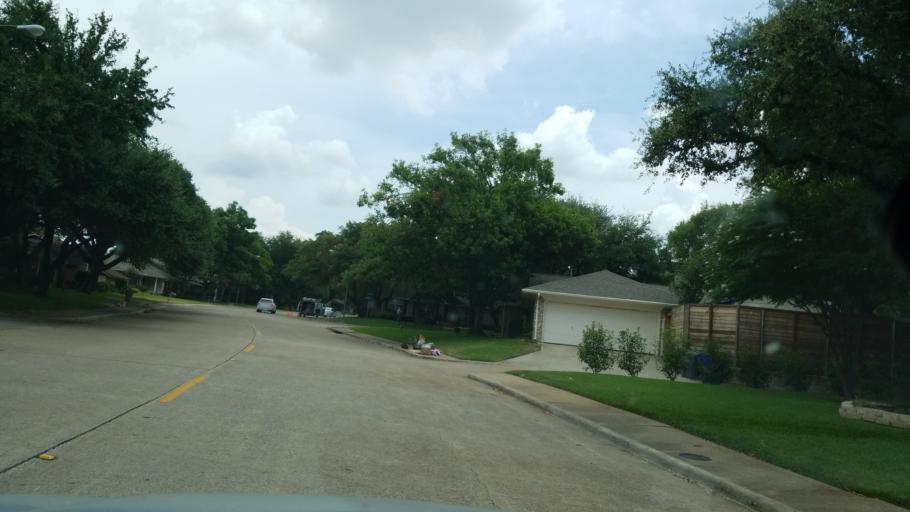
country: US
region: Texas
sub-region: Dallas County
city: Richardson
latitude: 32.8922
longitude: -96.7212
